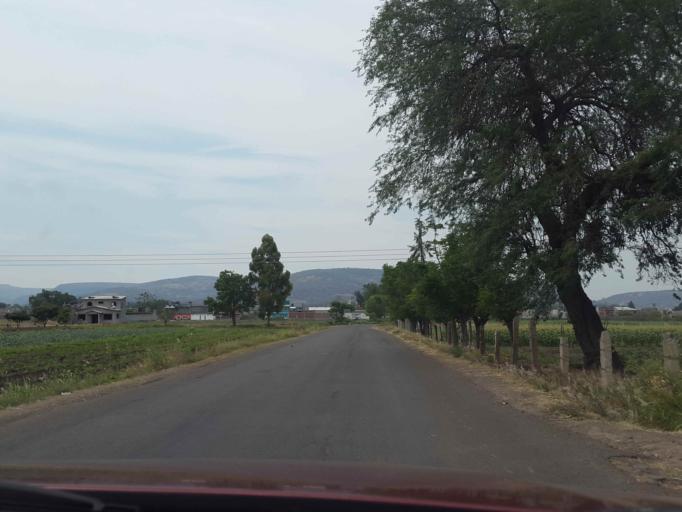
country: MX
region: Michoacan
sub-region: Tarimbaro
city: El Colegio
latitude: 19.7868
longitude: -101.1778
